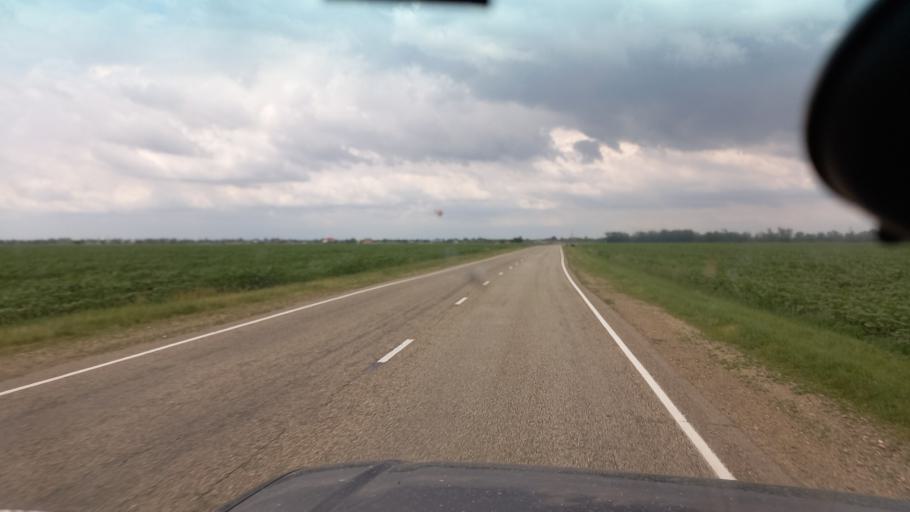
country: RU
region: Adygeya
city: Koshekhabl'
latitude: 44.8742
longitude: 40.5090
